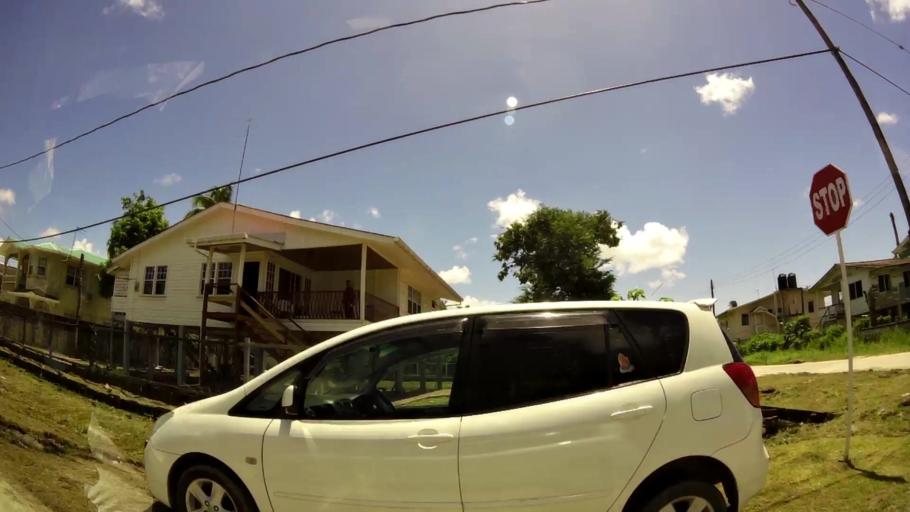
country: GY
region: Demerara-Mahaica
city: Georgetown
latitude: 6.7878
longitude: -58.1501
